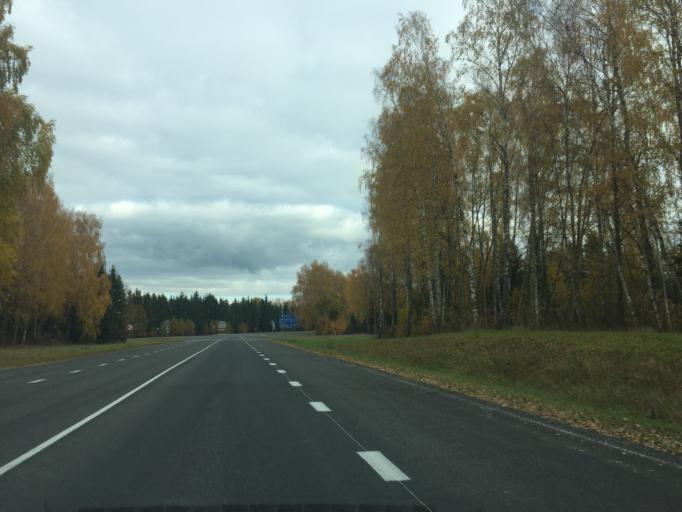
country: BY
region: Minsk
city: Svir
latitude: 54.8908
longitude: 26.3865
